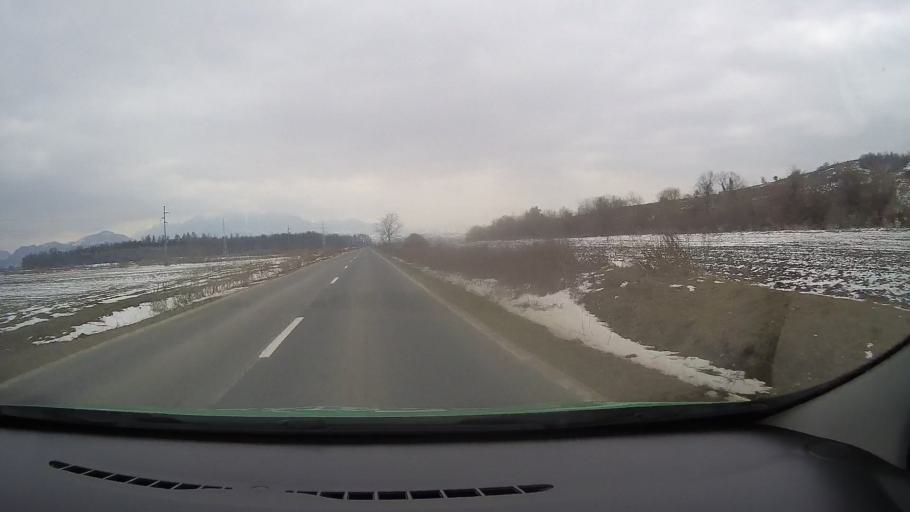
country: RO
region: Brasov
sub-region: Comuna Vulcan
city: Vulcan
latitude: 45.6019
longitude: 25.4203
